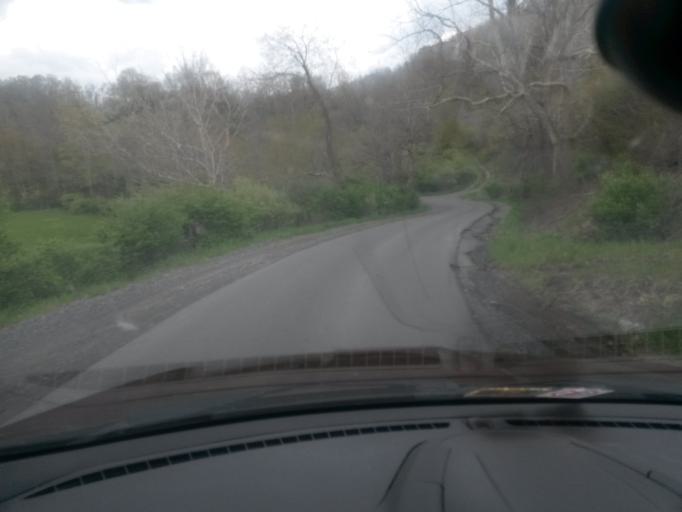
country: US
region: West Virginia
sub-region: Greenbrier County
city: Lewisburg
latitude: 37.9375
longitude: -80.4265
